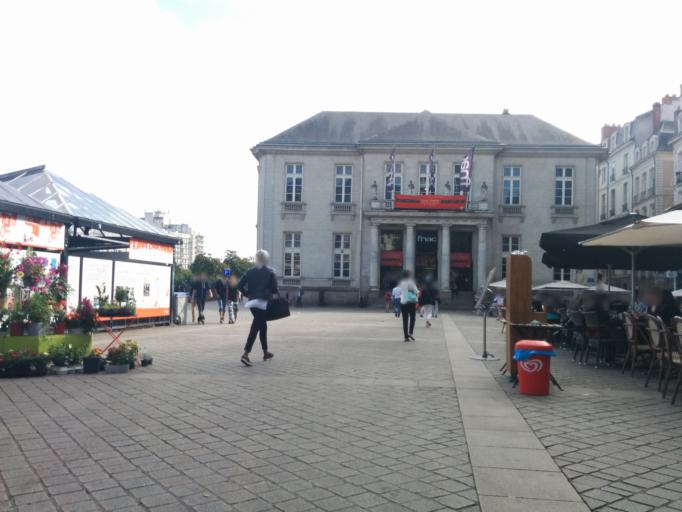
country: FR
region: Pays de la Loire
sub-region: Departement de la Loire-Atlantique
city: Nantes
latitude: 47.2135
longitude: -1.5578
